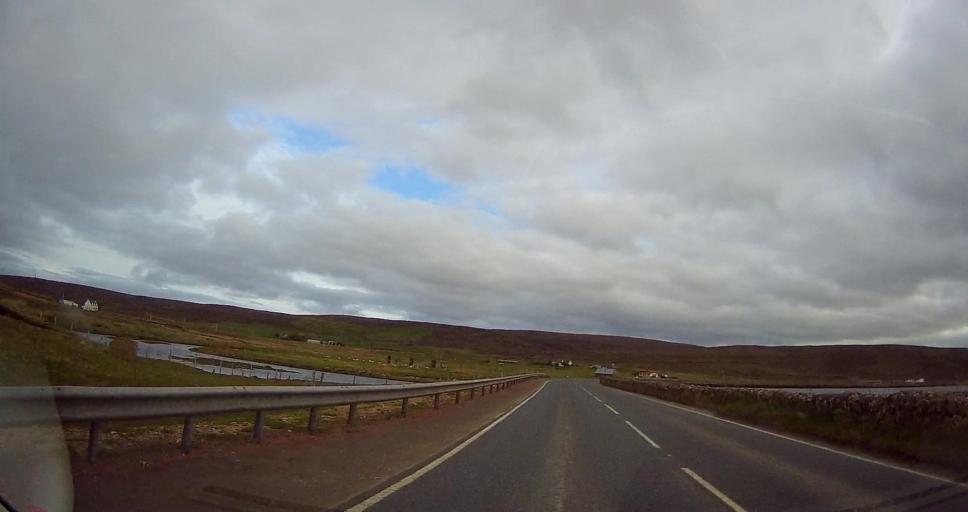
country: GB
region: Scotland
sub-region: Shetland Islands
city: Lerwick
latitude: 60.4469
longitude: -1.2596
